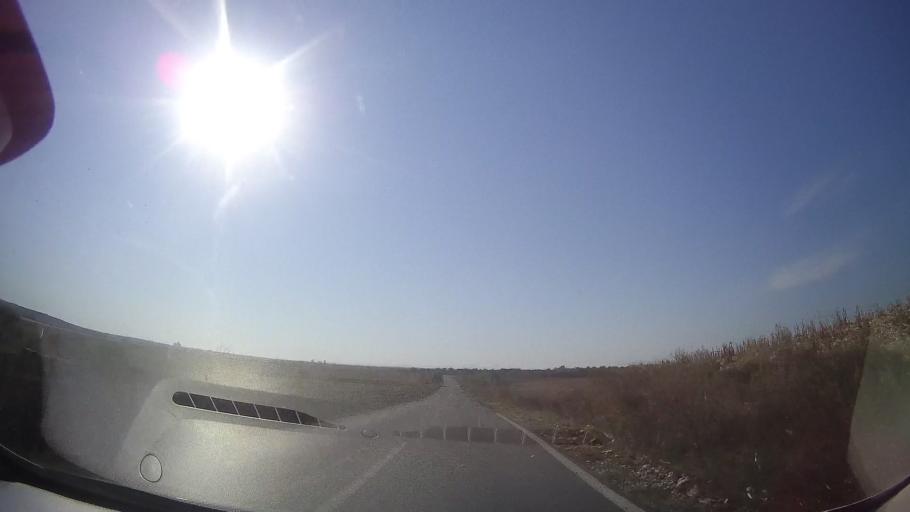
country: RO
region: Timis
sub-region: Comuna Topolovatu Mare
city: Topolovatu Mare
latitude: 45.7999
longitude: 21.5862
